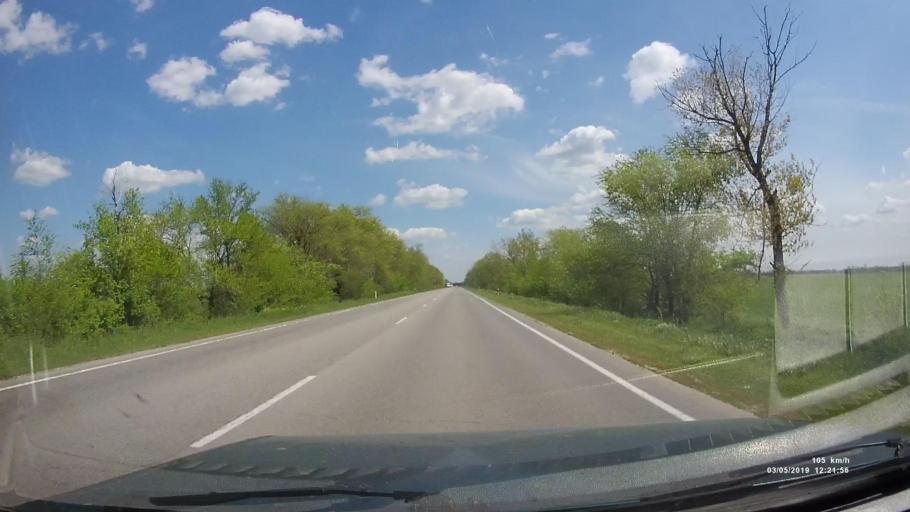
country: RU
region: Rostov
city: Melikhovskaya
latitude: 47.4057
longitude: 40.6495
